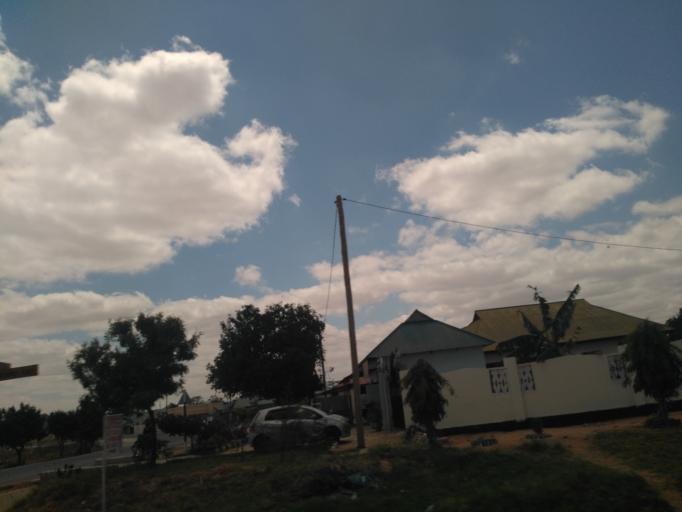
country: TZ
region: Dodoma
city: Kisasa
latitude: -6.1767
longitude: 35.7936
